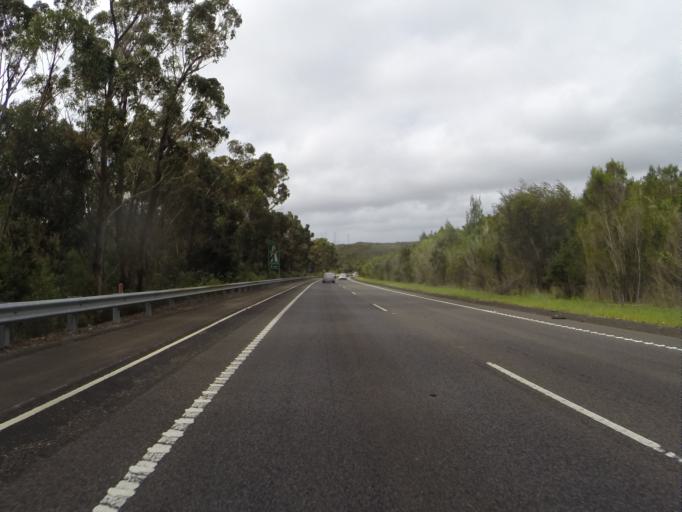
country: AU
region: New South Wales
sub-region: Wollongong
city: Helensburgh
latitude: -34.1668
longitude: 150.9785
